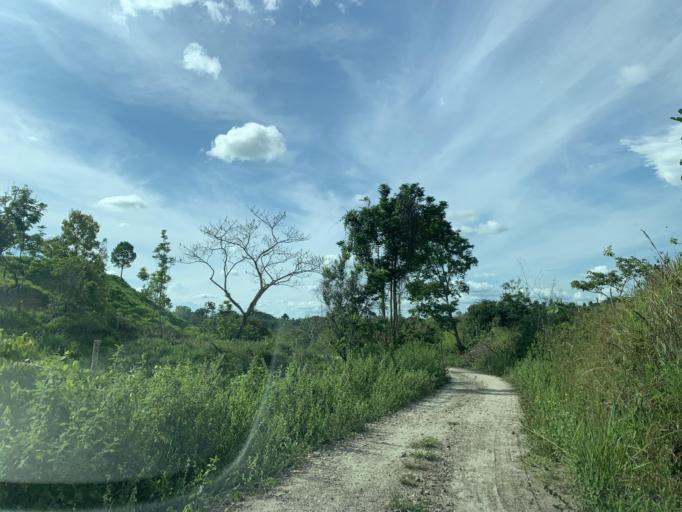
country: CO
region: Boyaca
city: Puerto Boyaca
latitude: 6.0071
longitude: -74.3820
